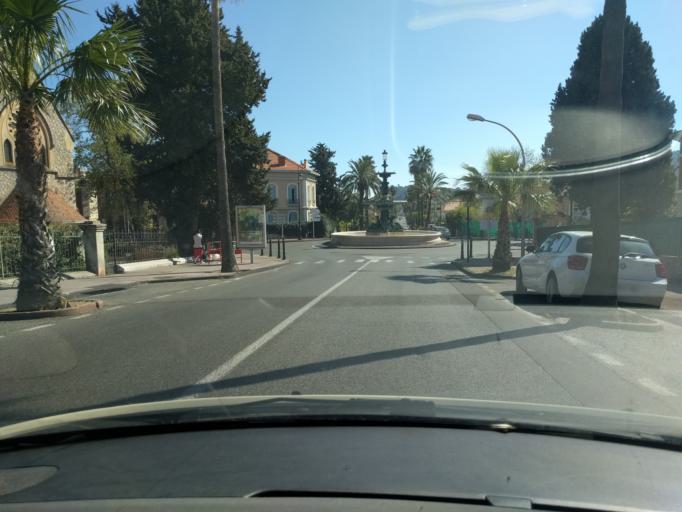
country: FR
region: Provence-Alpes-Cote d'Azur
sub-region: Departement du Var
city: Hyeres
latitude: 43.1181
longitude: 6.1223
